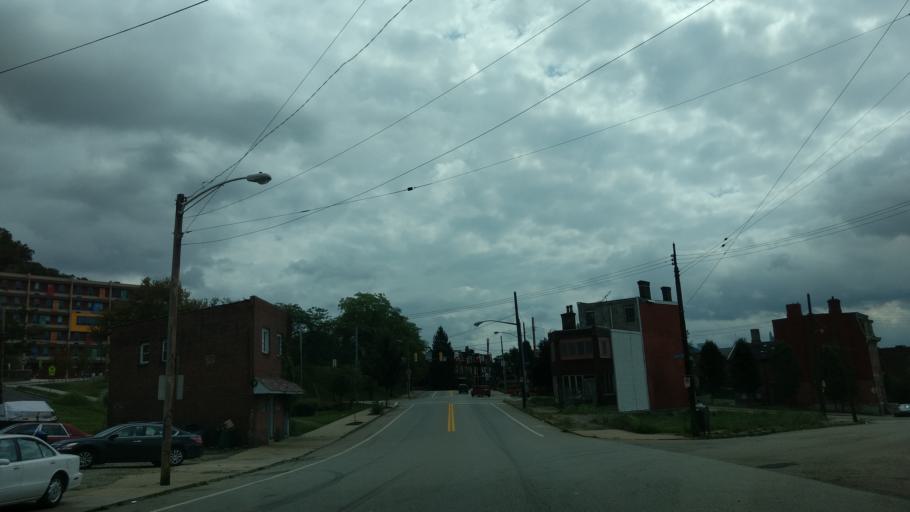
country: US
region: Pennsylvania
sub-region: Allegheny County
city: Pittsburgh
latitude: 40.4602
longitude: -80.0181
